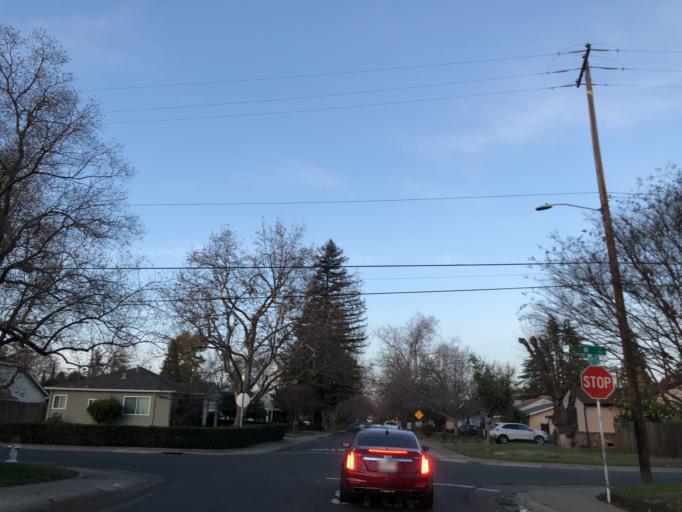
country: US
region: California
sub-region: Sacramento County
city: Sacramento
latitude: 38.5607
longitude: -121.4357
